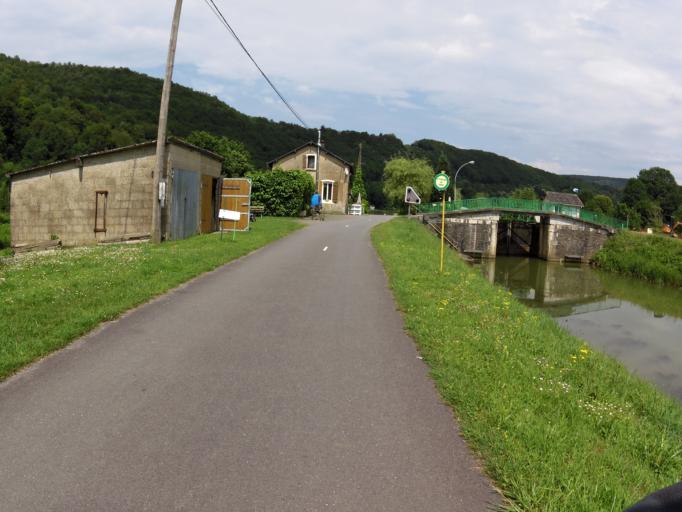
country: FR
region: Champagne-Ardenne
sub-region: Departement des Ardennes
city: Nouzonville
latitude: 49.8372
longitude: 4.7536
